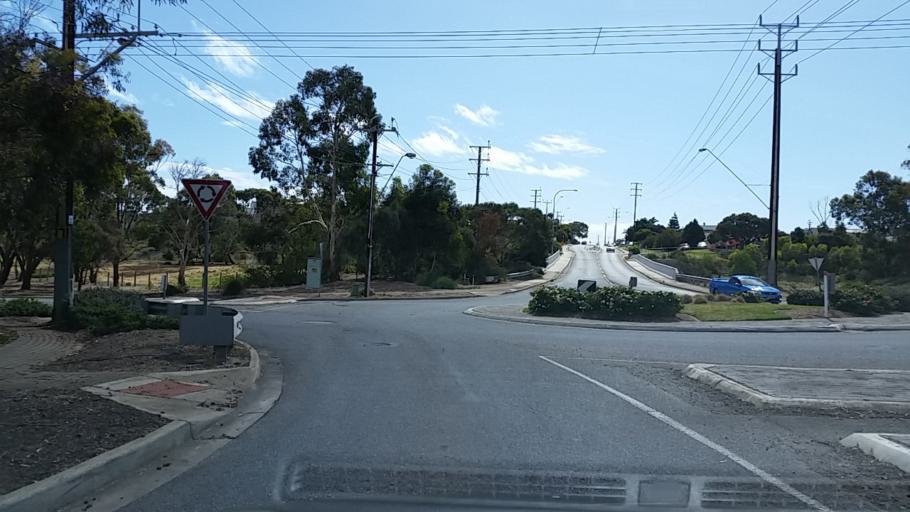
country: AU
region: South Australia
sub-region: Onkaparinga
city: Morphett Vale
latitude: -35.1164
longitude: 138.5105
